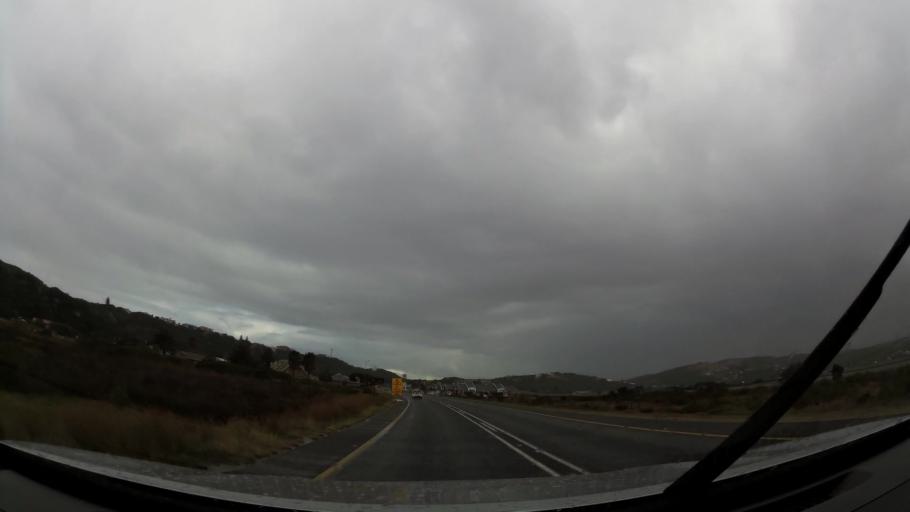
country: ZA
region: Western Cape
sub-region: Eden District Municipality
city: Mossel Bay
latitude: -34.0525
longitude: 22.2284
